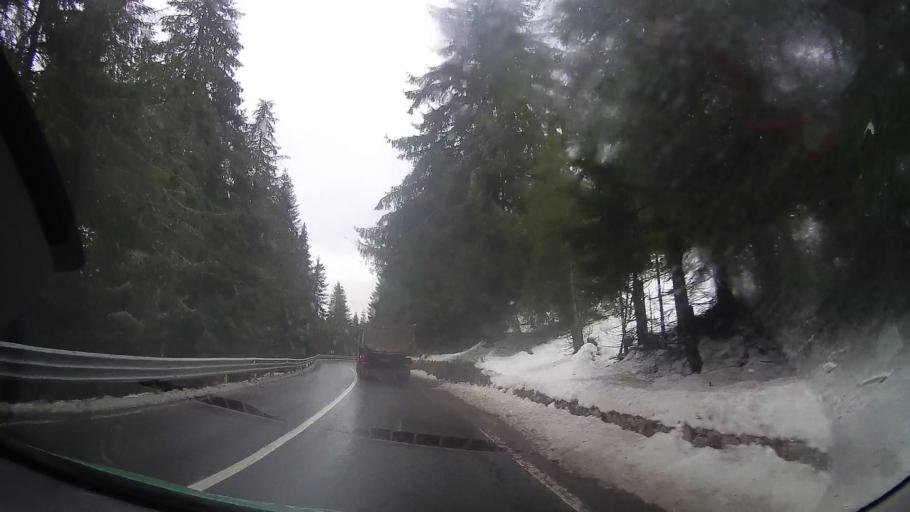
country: RO
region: Harghita
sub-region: Municipiul Gheorgheni
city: Gheorgheni
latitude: 46.7787
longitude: 25.7200
